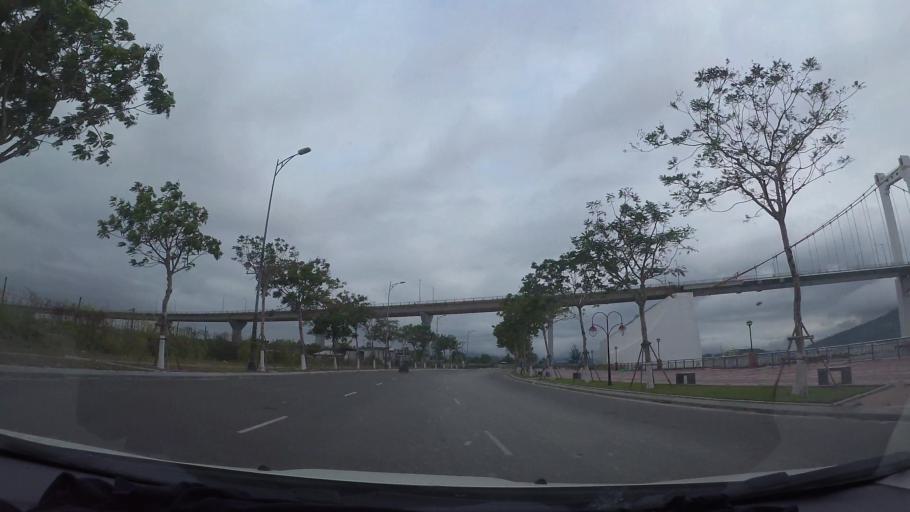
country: VN
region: Da Nang
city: Da Nang
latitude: 16.0924
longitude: 108.2179
